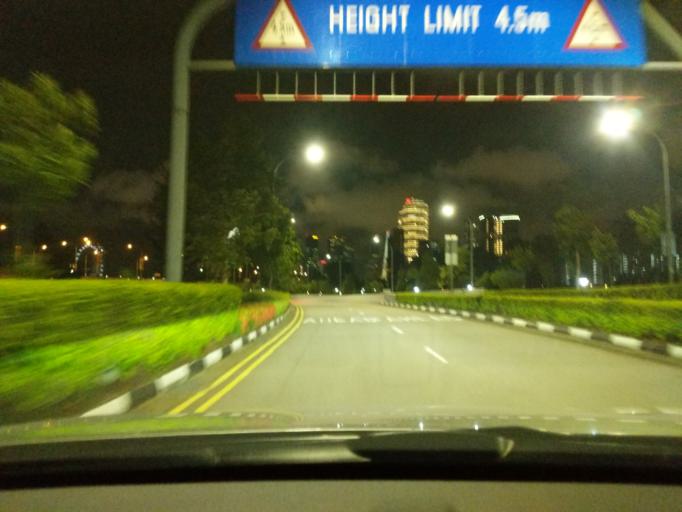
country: SG
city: Singapore
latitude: 1.3063
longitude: 103.8700
